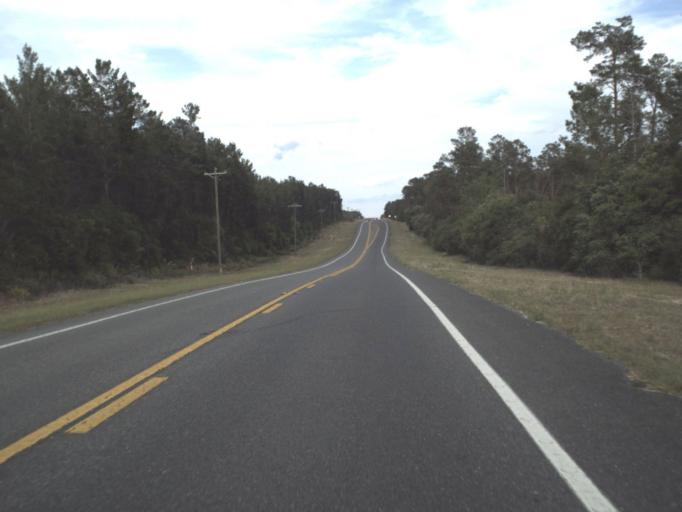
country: US
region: Florida
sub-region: Marion County
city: Silver Springs Shores
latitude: 29.1764
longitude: -81.8212
